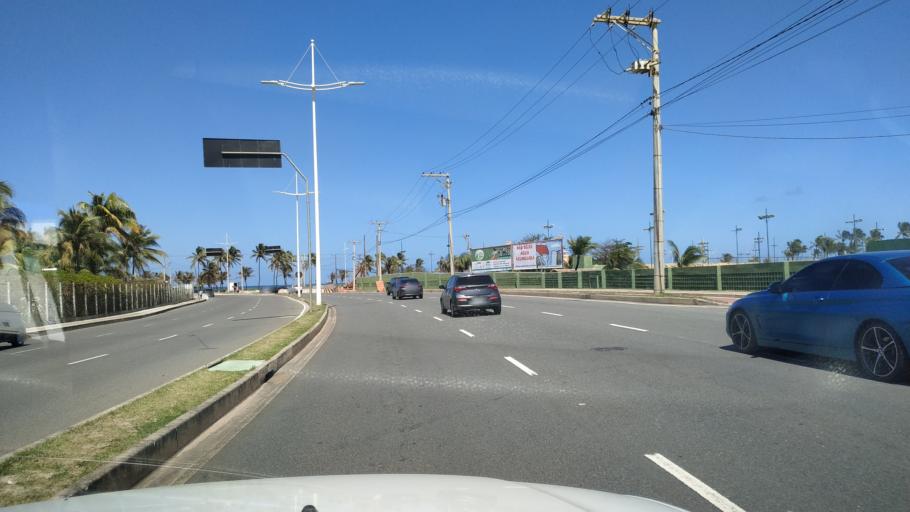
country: BR
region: Bahia
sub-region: Lauro De Freitas
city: Lauro de Freitas
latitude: -12.9528
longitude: -38.3852
